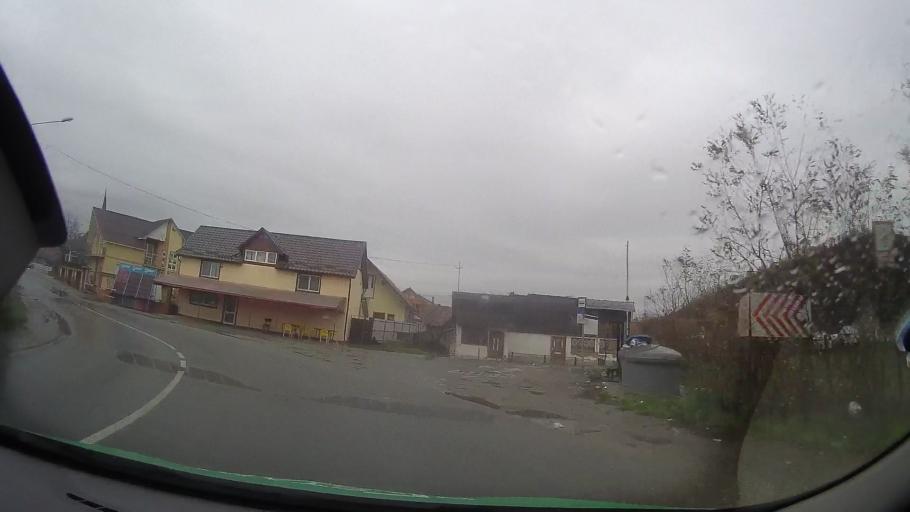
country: RO
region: Bistrita-Nasaud
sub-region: Municipiul Bistrita
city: Viisoara
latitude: 47.0701
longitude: 24.4373
